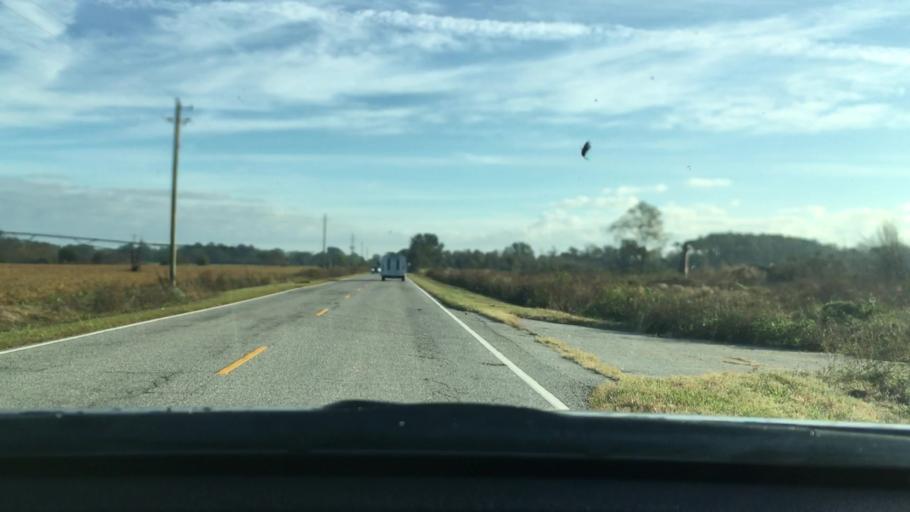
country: US
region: South Carolina
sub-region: Sumter County
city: East Sumter
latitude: 34.0611
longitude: -80.2279
